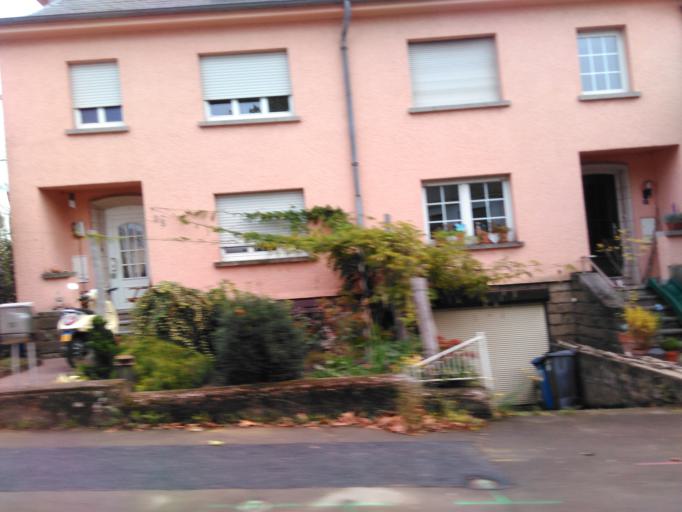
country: LU
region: Luxembourg
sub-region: Canton d'Esch-sur-Alzette
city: Esch-sur-Alzette
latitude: 49.5015
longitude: 5.9688
